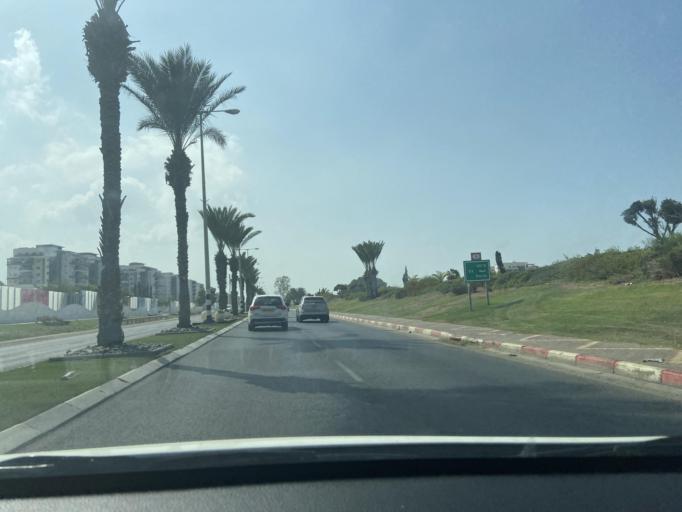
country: IL
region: Northern District
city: Nahariya
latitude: 33.0038
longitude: 35.0990
